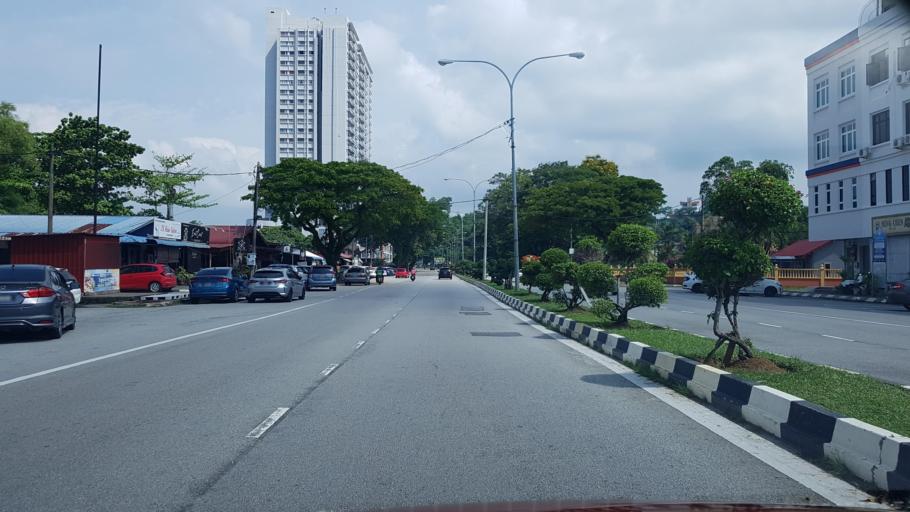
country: MY
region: Terengganu
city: Kuala Terengganu
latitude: 5.3246
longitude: 103.1416
